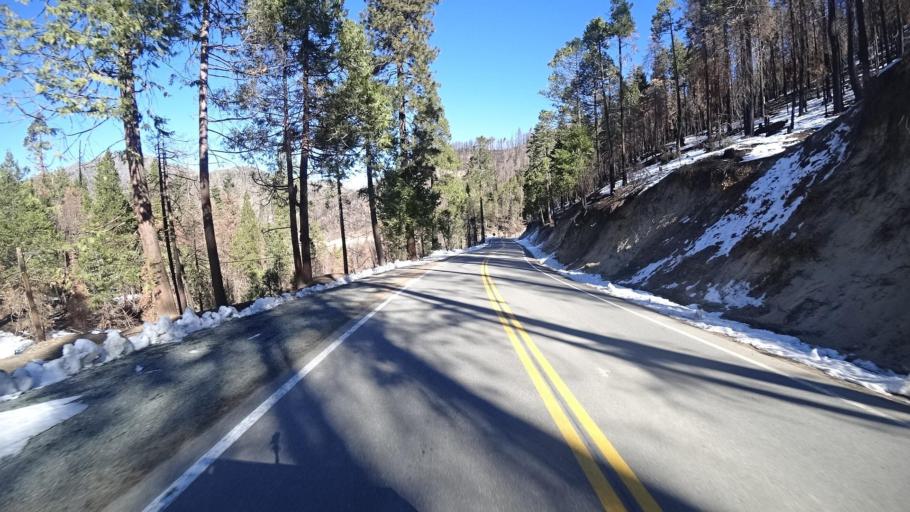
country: US
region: California
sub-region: Kern County
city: Alta Sierra
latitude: 35.7440
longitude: -118.5567
